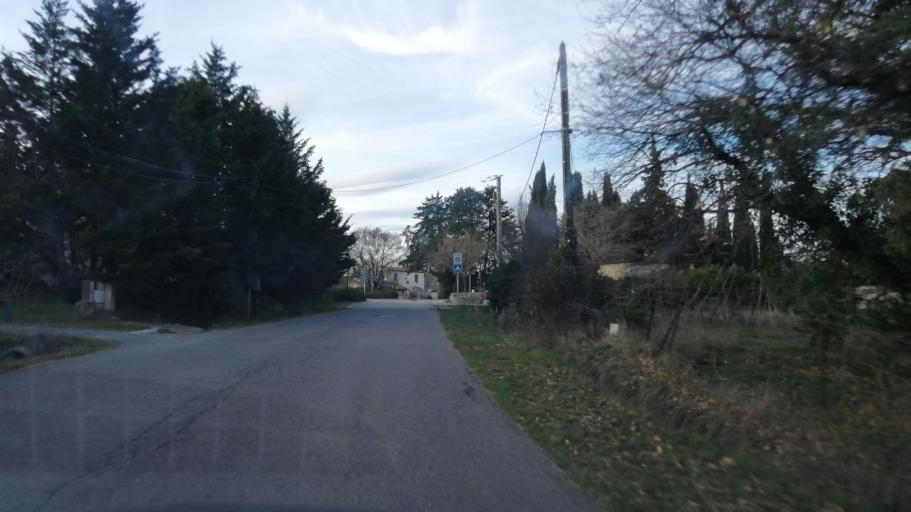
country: FR
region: Languedoc-Roussillon
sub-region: Departement de l'Herault
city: Claret
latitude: 43.8365
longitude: 3.9213
